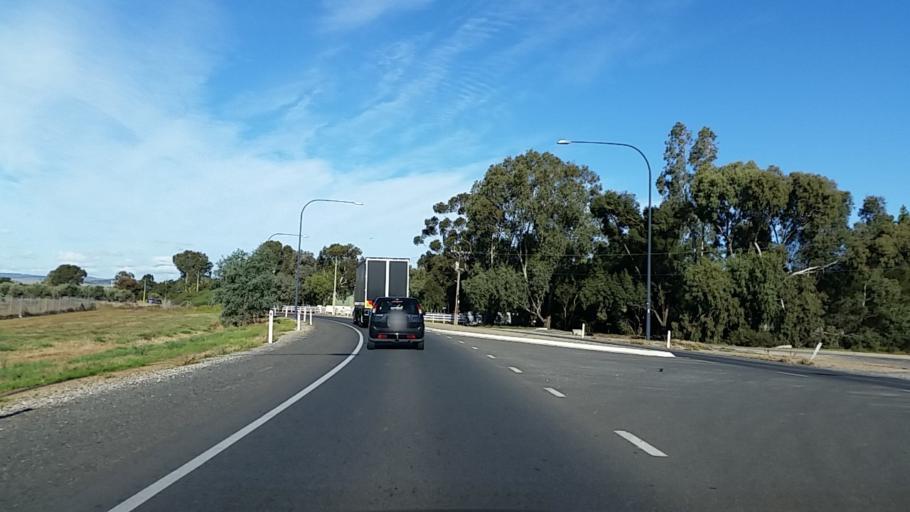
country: AU
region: South Australia
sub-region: Playford
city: Angle Vale
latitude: -34.6829
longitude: 138.6233
